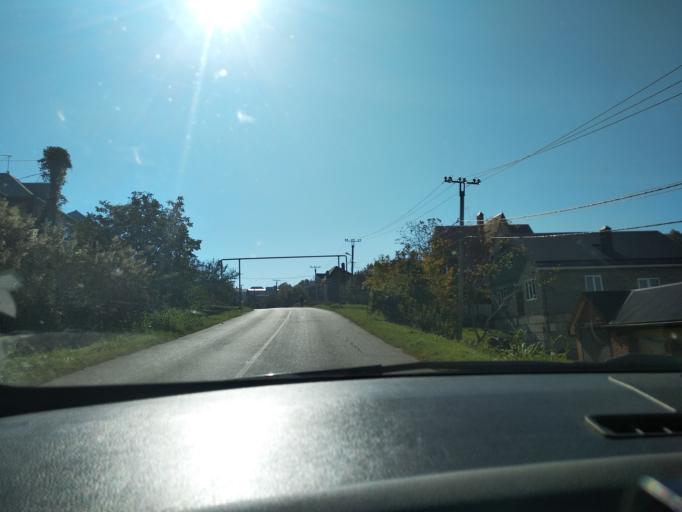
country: RU
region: Krasnodarskiy
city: Goryachiy Klyuch
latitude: 44.6277
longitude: 39.1568
